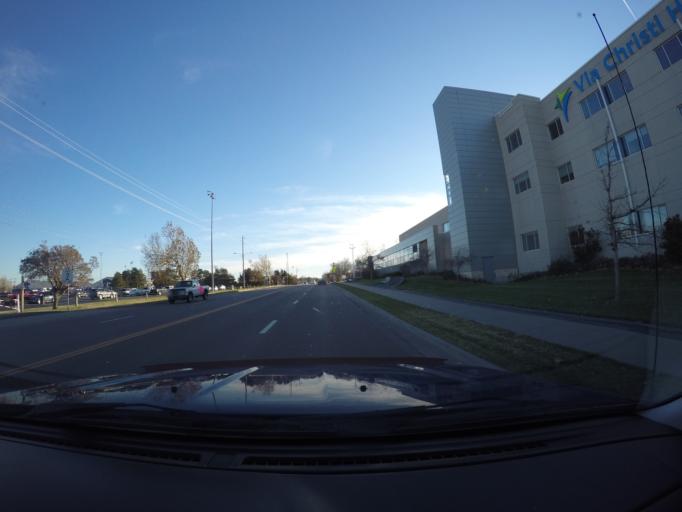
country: US
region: Kansas
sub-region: Riley County
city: Manhattan
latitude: 39.2016
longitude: -96.5983
